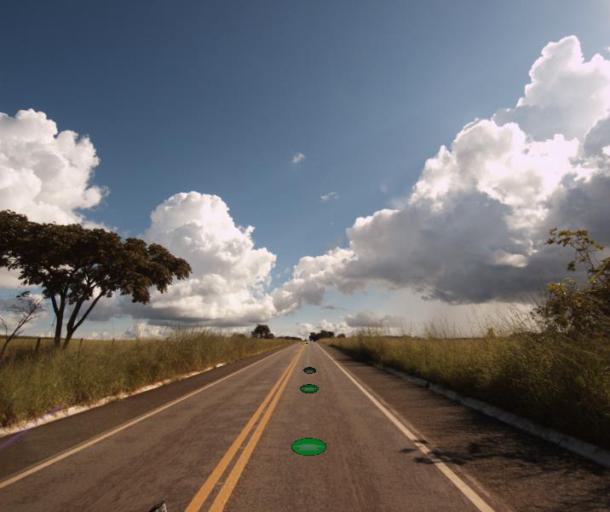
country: BR
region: Goias
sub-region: Itaberai
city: Itaberai
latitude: -15.9737
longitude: -49.6769
